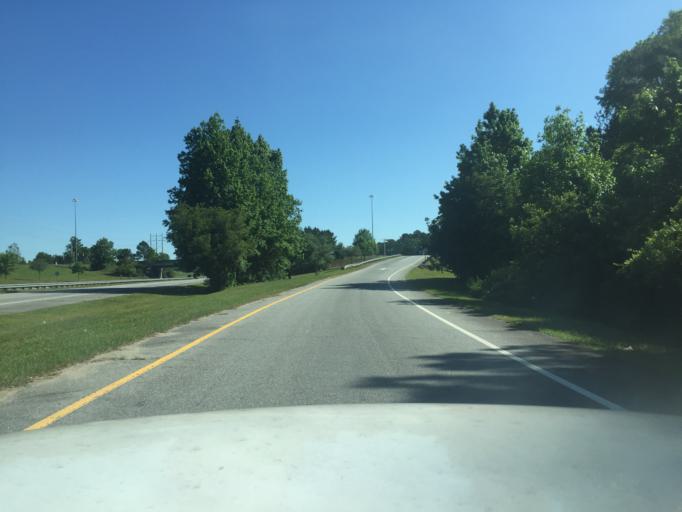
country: US
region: Georgia
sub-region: Chatham County
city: Garden City
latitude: 32.0367
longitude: -81.1648
